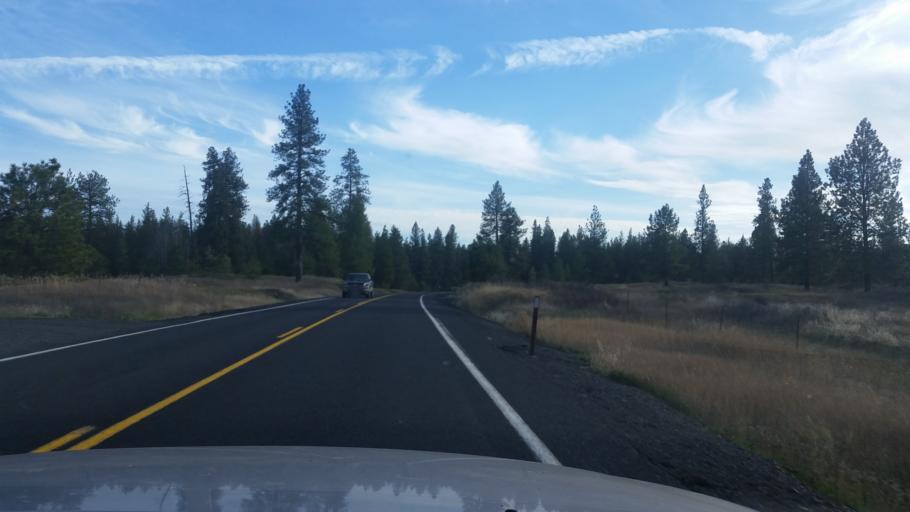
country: US
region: Washington
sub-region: Spokane County
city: Cheney
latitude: 47.4537
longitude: -117.5770
